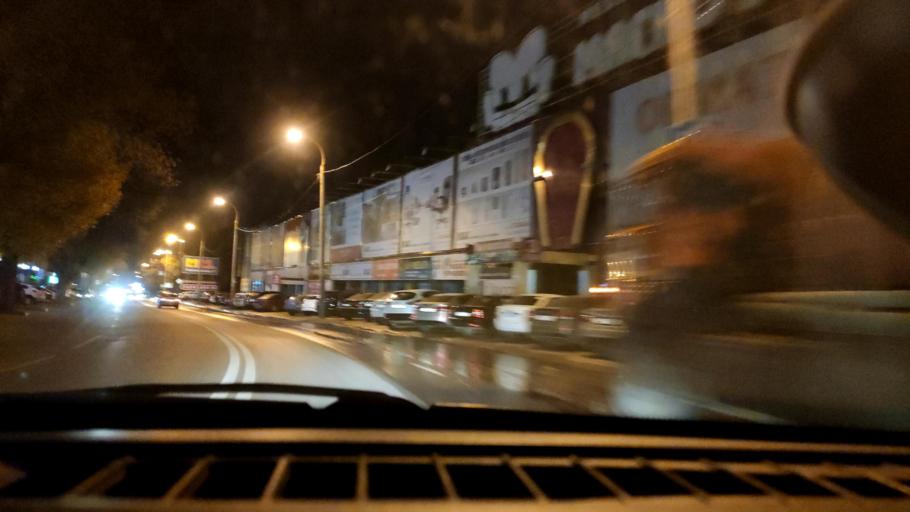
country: RU
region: Samara
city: Samara
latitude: 53.2060
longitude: 50.1780
